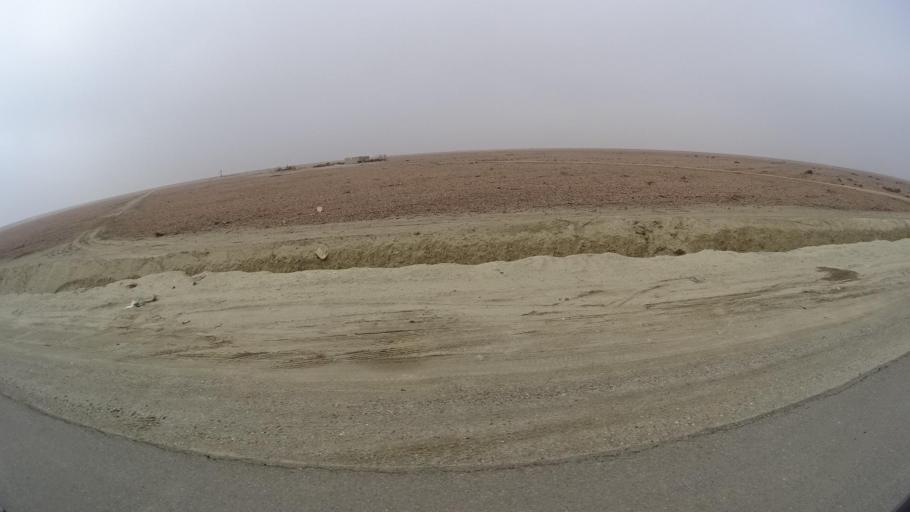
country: US
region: California
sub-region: Kern County
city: Greenfield
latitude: 35.0808
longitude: -119.1224
